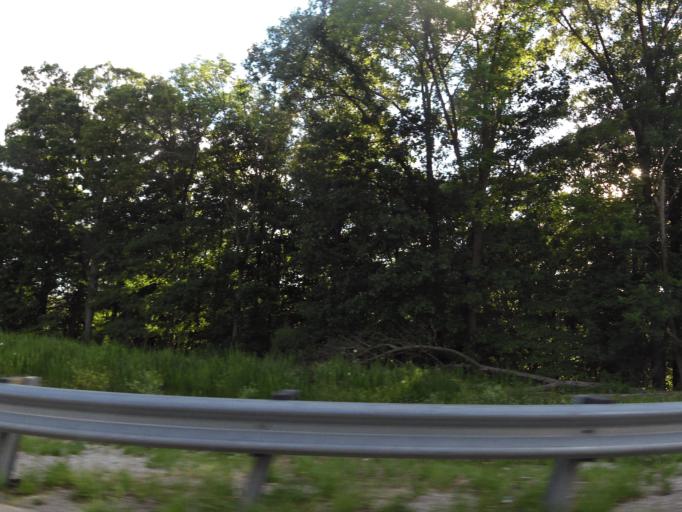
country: US
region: Missouri
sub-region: Saint Charles County
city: Weldon Spring
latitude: 38.6953
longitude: -90.6659
